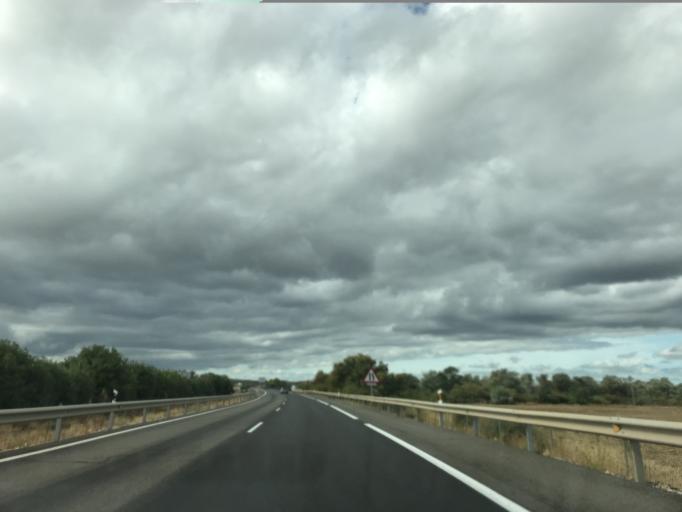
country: ES
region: Andalusia
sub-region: Province of Cordoba
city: Villa del Rio
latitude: 37.9873
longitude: -4.2905
